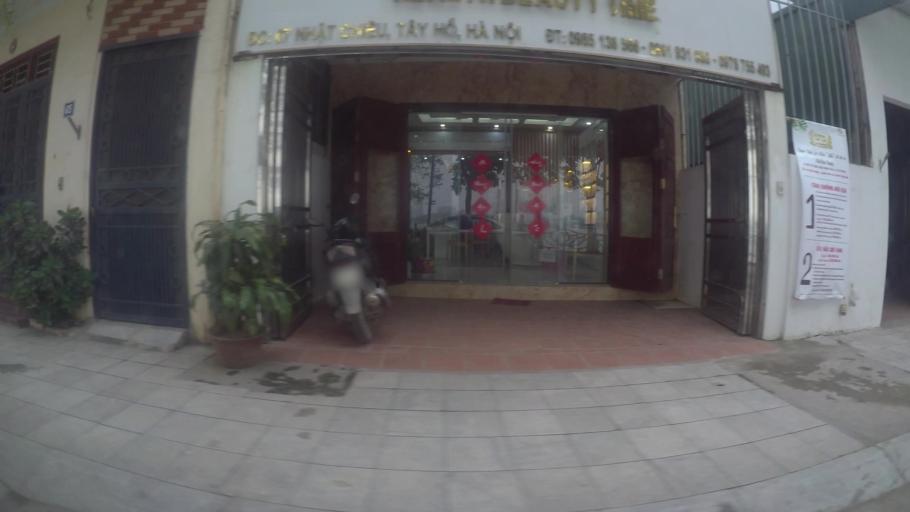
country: VN
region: Ha Noi
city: Tay Ho
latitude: 21.0709
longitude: 105.8138
